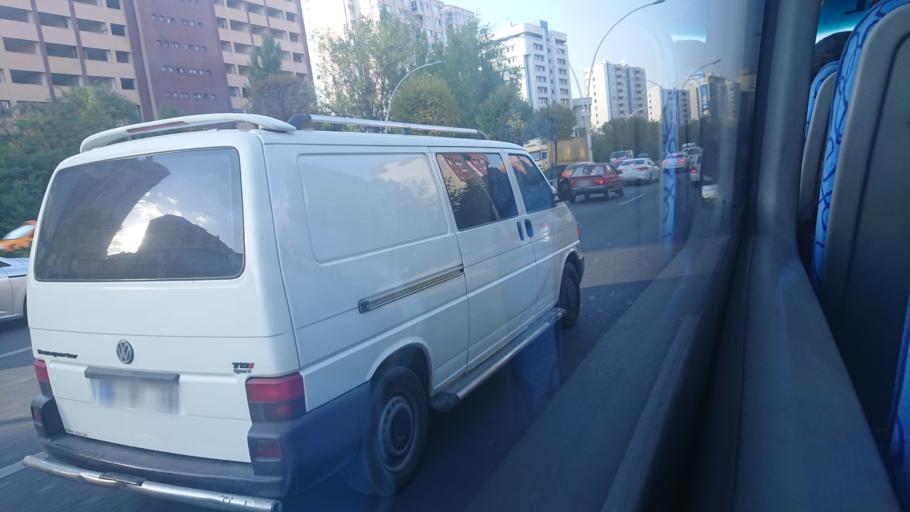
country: TR
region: Ankara
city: Ankara
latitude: 39.9252
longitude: 32.8155
